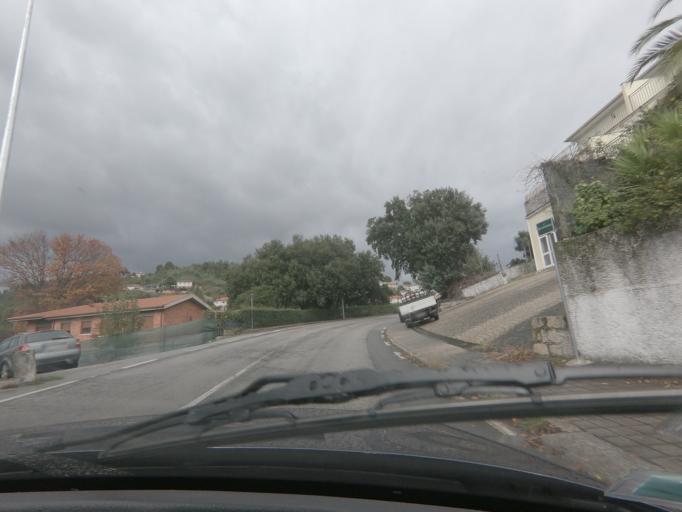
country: PT
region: Vila Real
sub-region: Mondim de Basto
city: Mondim de Basto
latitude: 41.4045
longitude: -7.9572
